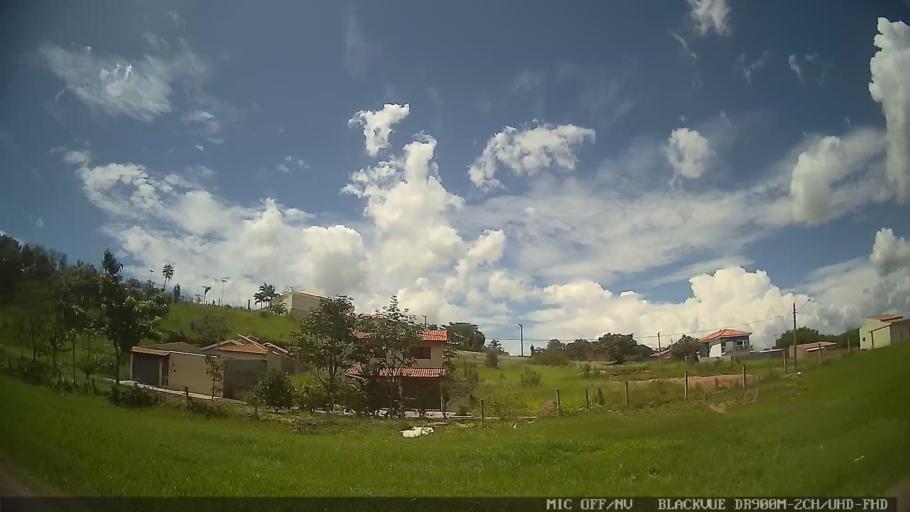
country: BR
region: Sao Paulo
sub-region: Conchas
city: Conchas
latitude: -23.0257
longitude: -48.0057
